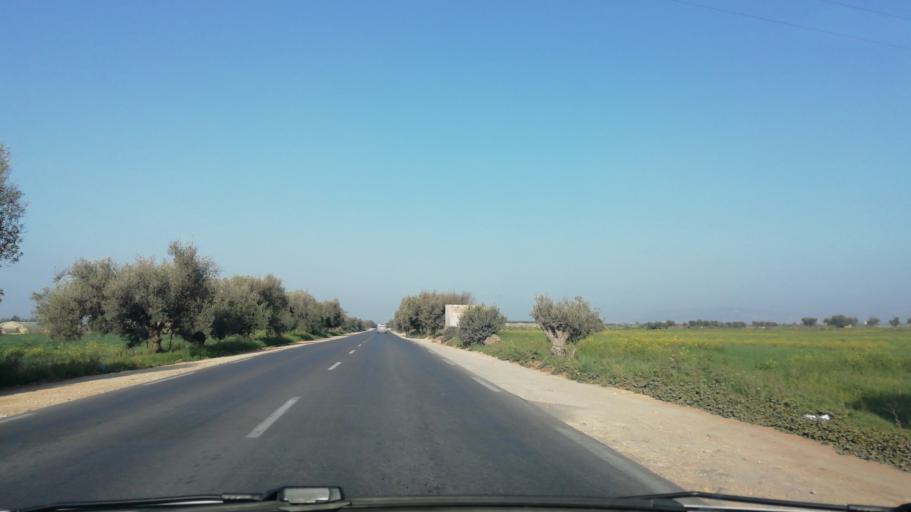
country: DZ
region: Mostaganem
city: Mostaganem
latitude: 35.7484
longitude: 0.1326
